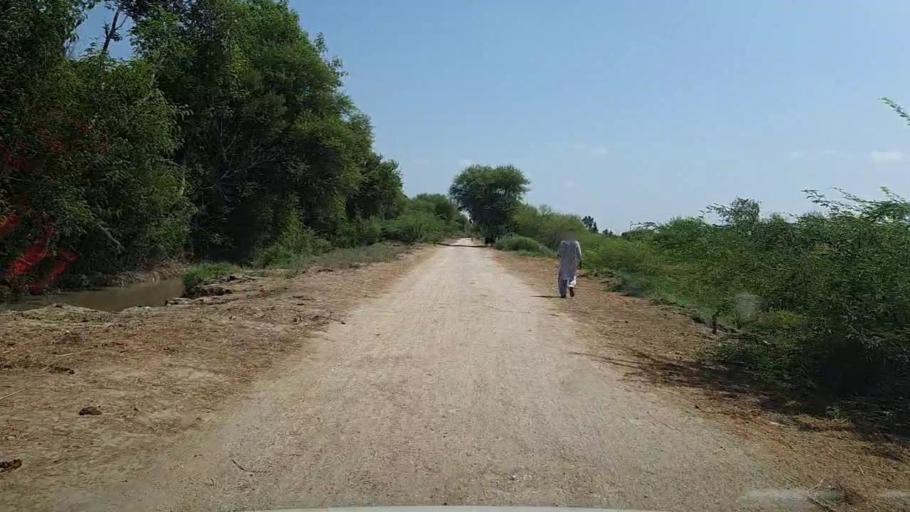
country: PK
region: Sindh
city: Kario
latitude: 24.8487
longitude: 68.6936
